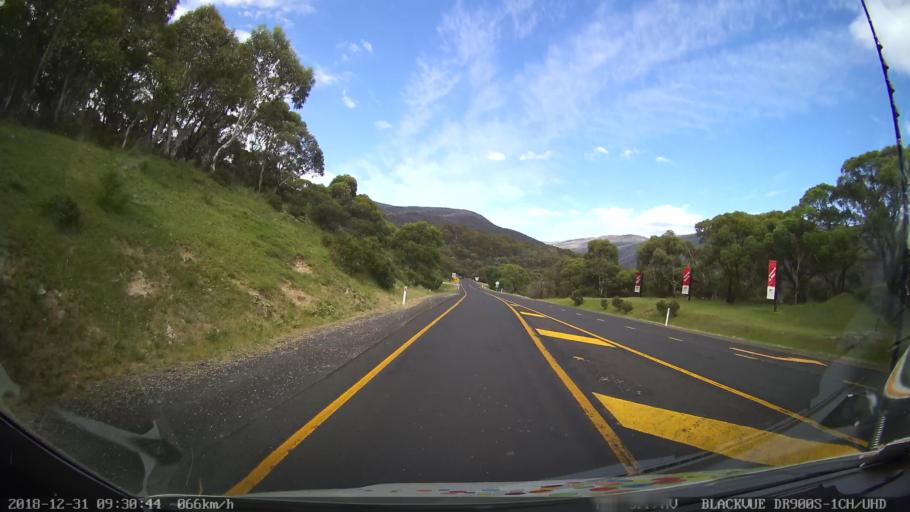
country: AU
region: New South Wales
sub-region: Snowy River
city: Jindabyne
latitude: -36.4496
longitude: 148.4510
